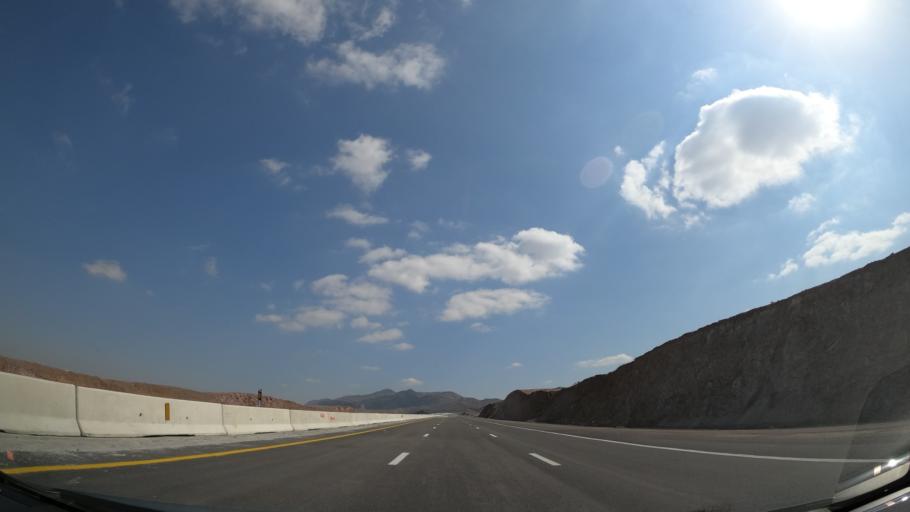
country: IR
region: Alborz
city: Nazarabad
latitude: 35.6995
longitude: 50.6229
